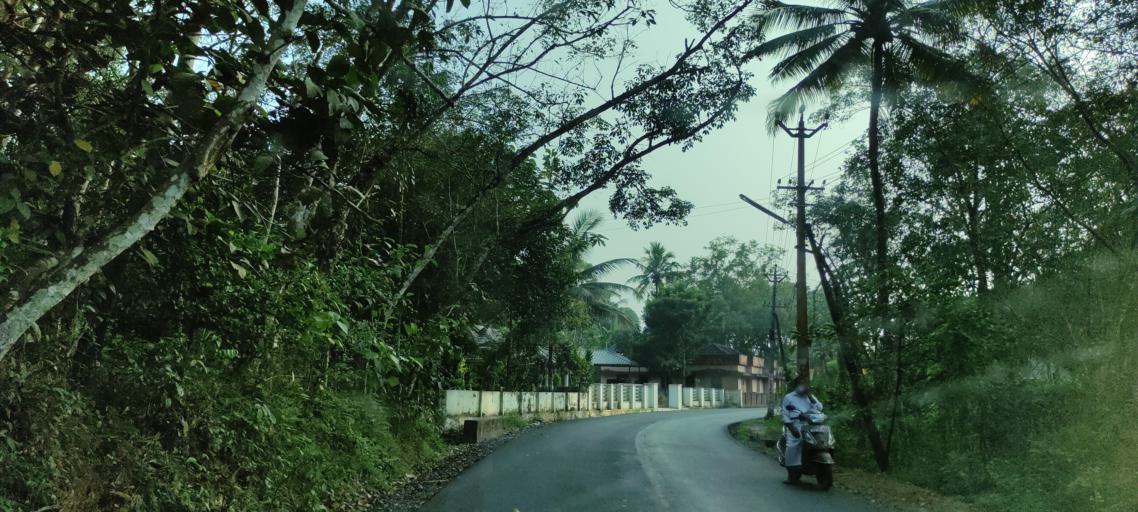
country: IN
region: Kerala
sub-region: Pattanamtitta
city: Adur
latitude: 9.1056
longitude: 76.7270
